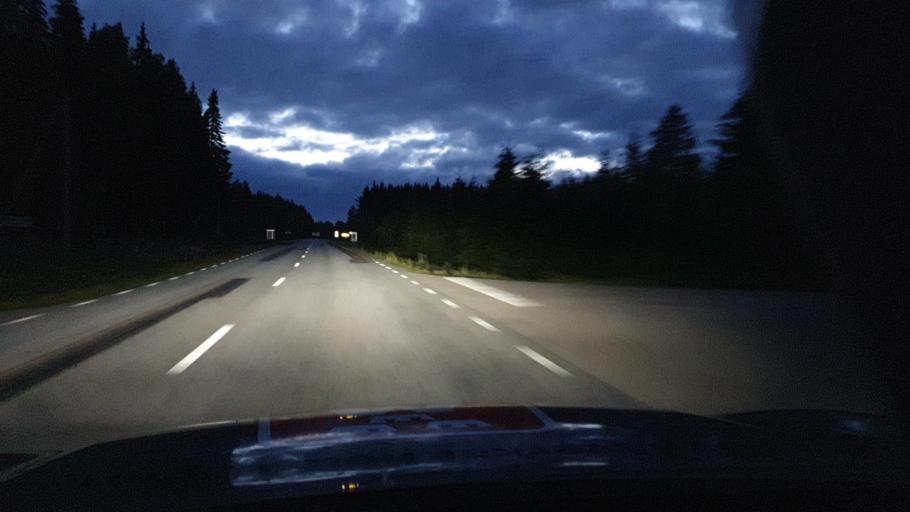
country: SE
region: OErebro
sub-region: Karlskoga Kommun
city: Karlskoga
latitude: 59.4448
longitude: 14.5130
